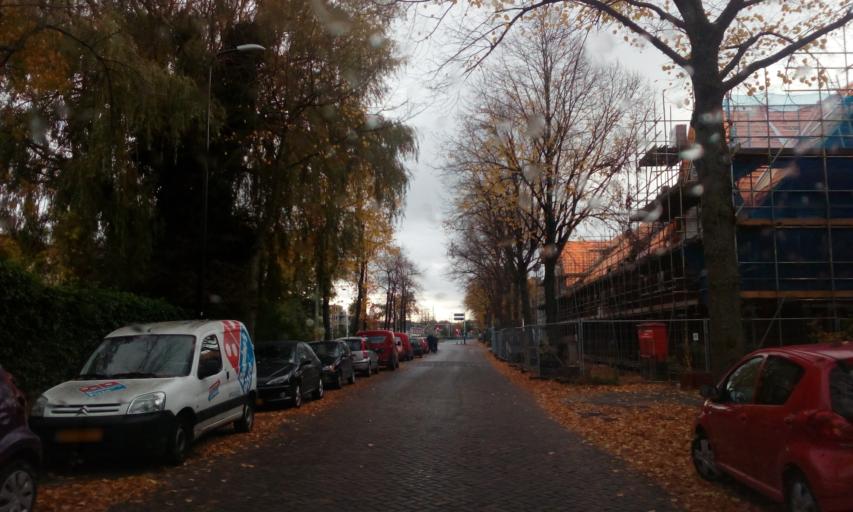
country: NL
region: South Holland
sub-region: Gemeente Delft
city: Delft
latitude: 52.0258
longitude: 4.3484
